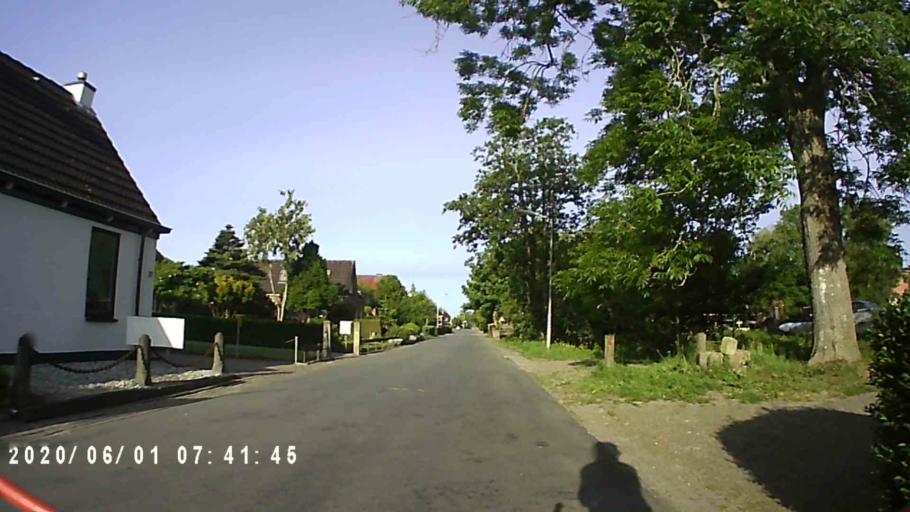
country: NL
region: Friesland
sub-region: Gemeente Dantumadiel
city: Damwald
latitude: 53.2921
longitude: 5.9818
